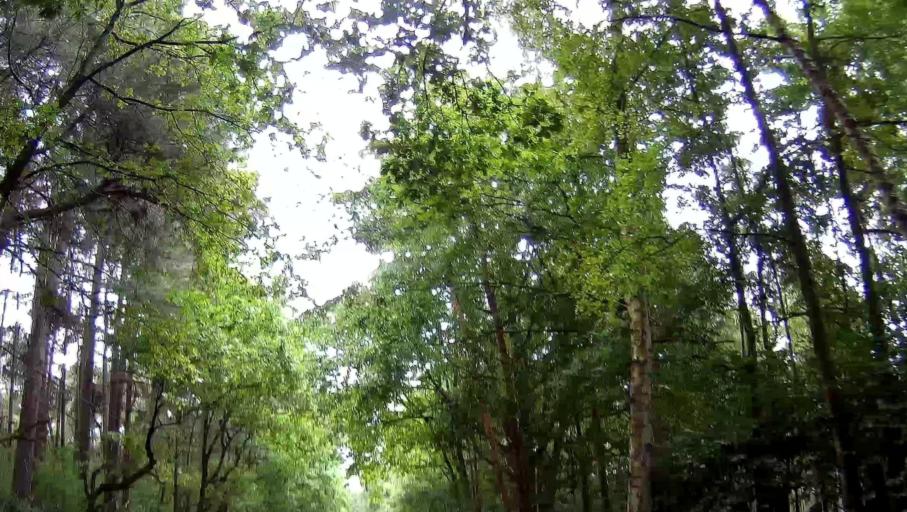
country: BE
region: Flanders
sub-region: Provincie Antwerpen
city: Balen
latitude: 51.2027
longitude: 5.2072
